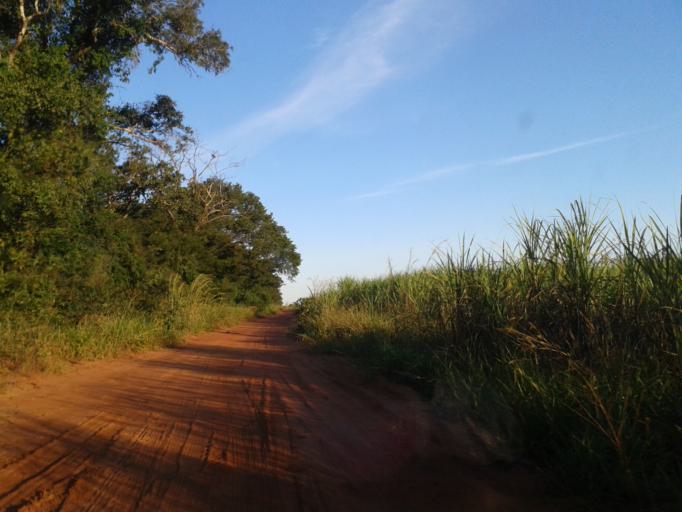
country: BR
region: Minas Gerais
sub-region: Santa Vitoria
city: Santa Vitoria
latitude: -19.0082
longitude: -50.3779
